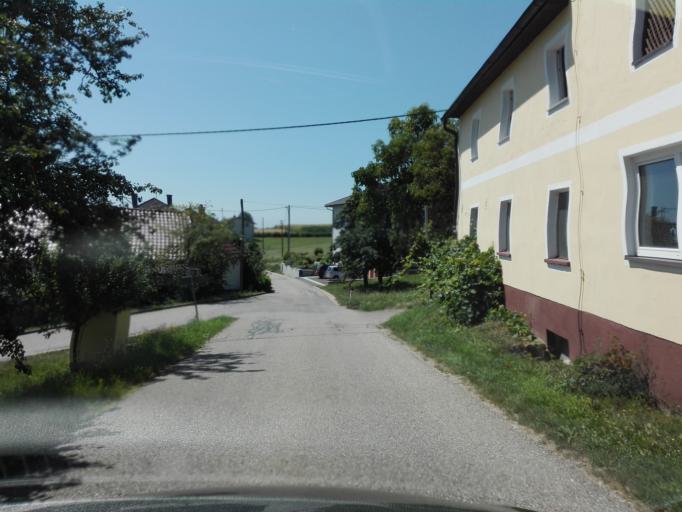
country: AT
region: Upper Austria
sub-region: Politischer Bezirk Urfahr-Umgebung
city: Engerwitzdorf
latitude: 48.2903
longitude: 14.4532
